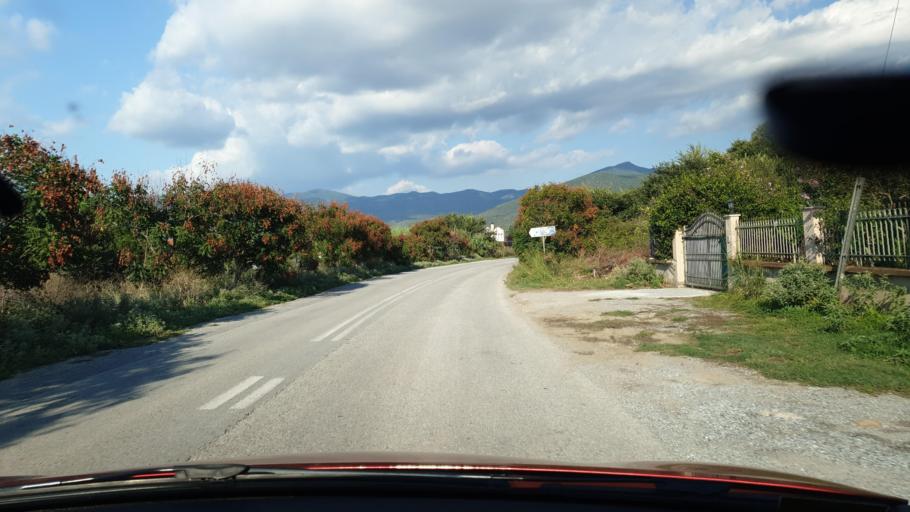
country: GR
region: Central Macedonia
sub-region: Nomos Thessalonikis
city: Vasilika
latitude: 40.4810
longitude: 23.1196
